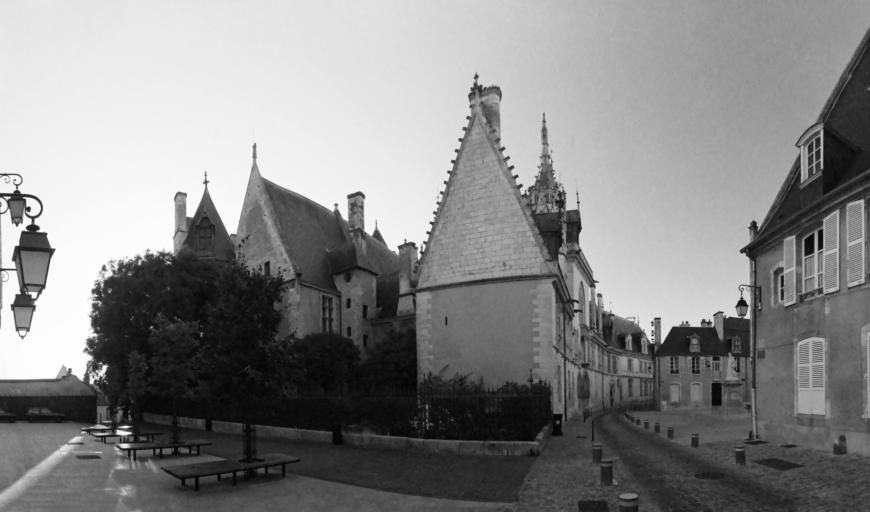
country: FR
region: Centre
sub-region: Departement du Cher
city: Bourges
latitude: 47.0840
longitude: 2.3941
